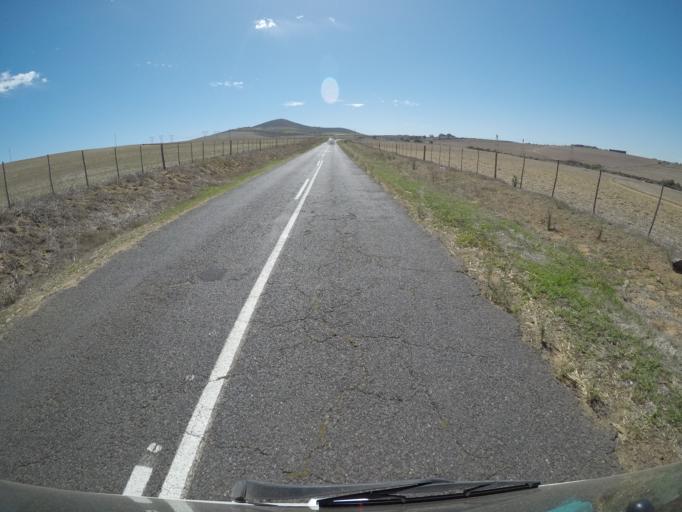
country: ZA
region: Western Cape
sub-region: City of Cape Town
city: Sunset Beach
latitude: -33.7366
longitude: 18.5660
